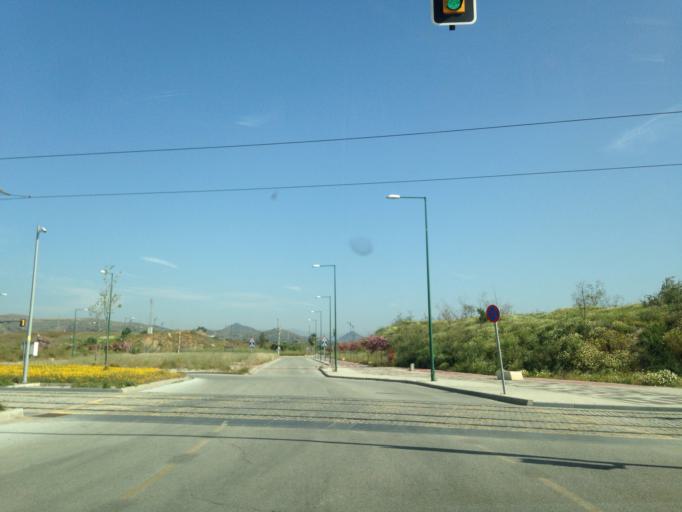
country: ES
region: Andalusia
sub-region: Provincia de Malaga
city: Malaga
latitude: 36.7182
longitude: -4.4949
